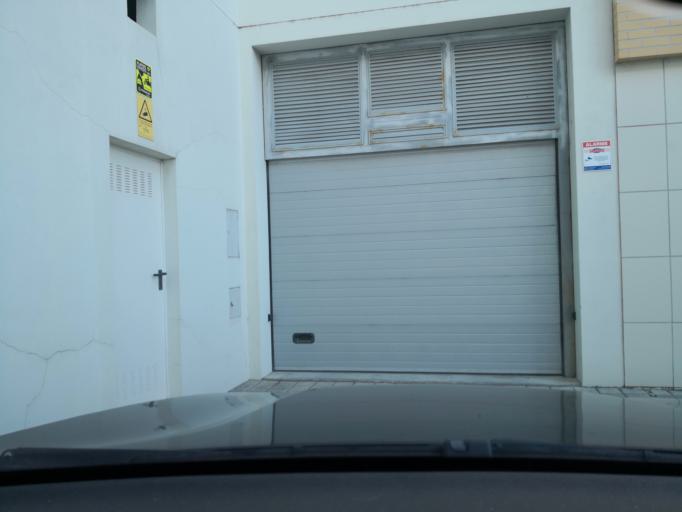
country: PT
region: Vila Real
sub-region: Vila Real
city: Vila Real
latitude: 41.3076
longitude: -7.7380
